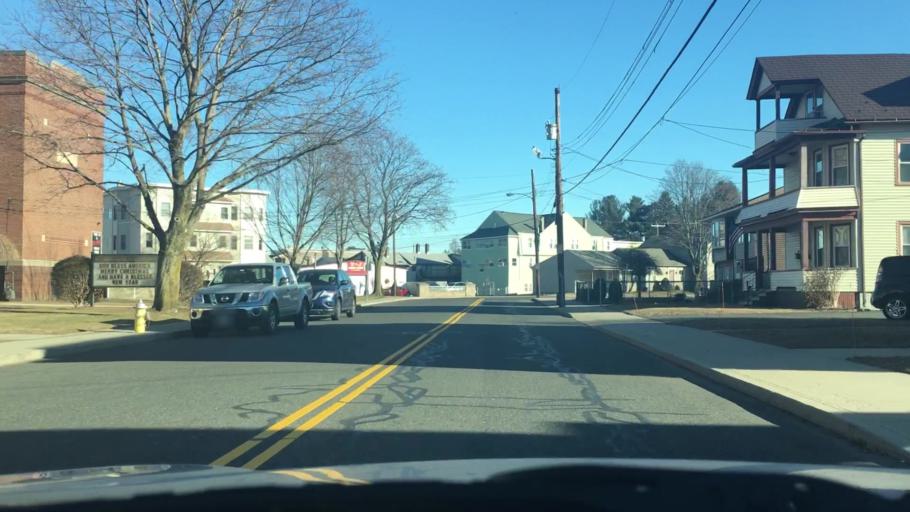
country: US
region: Massachusetts
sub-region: Hampden County
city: Ludlow
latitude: 42.1594
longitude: -72.4766
